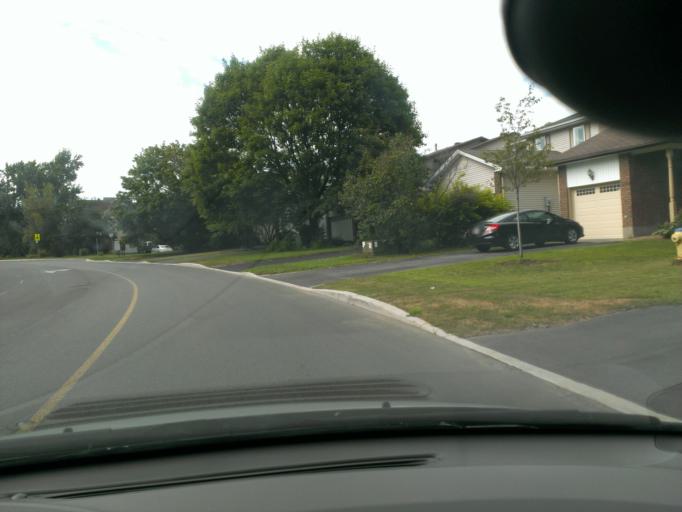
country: CA
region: Quebec
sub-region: Outaouais
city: Gatineau
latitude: 45.4778
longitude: -75.4930
